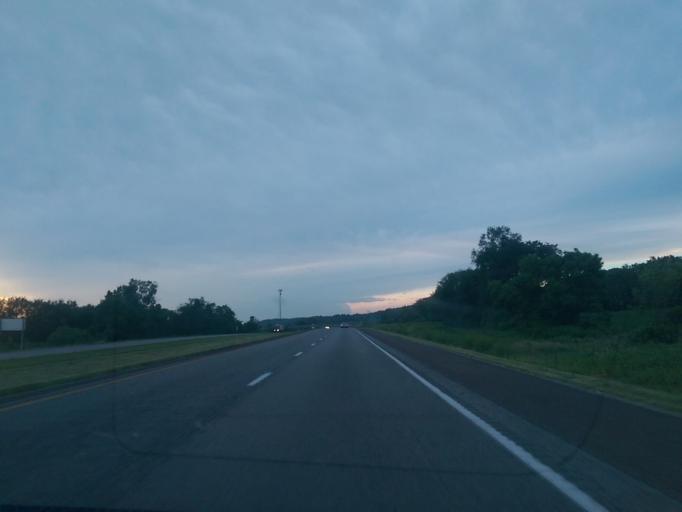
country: US
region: Missouri
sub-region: Holt County
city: Mound City
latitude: 40.2024
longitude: -95.3689
